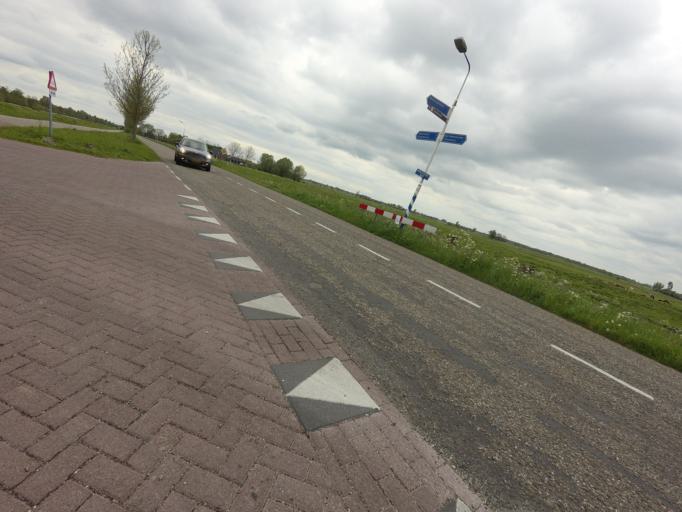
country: NL
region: Utrecht
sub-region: Stichtse Vecht
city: Maarssen
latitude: 52.1534
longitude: 5.0760
